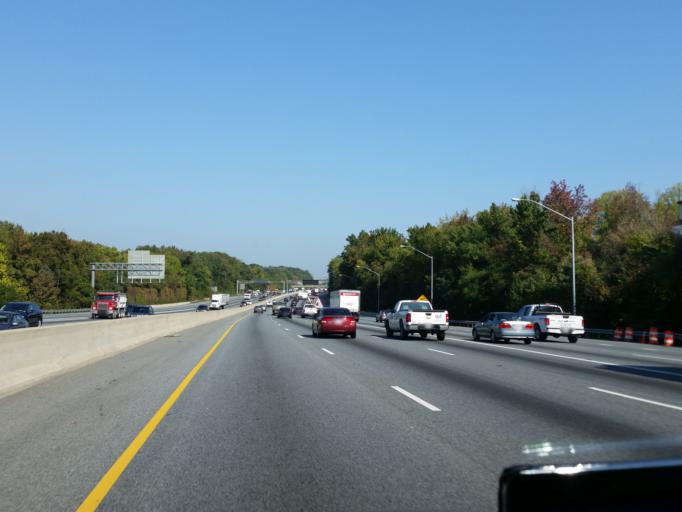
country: US
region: Maryland
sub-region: Prince George's County
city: Glenarden
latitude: 38.9226
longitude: -76.8532
